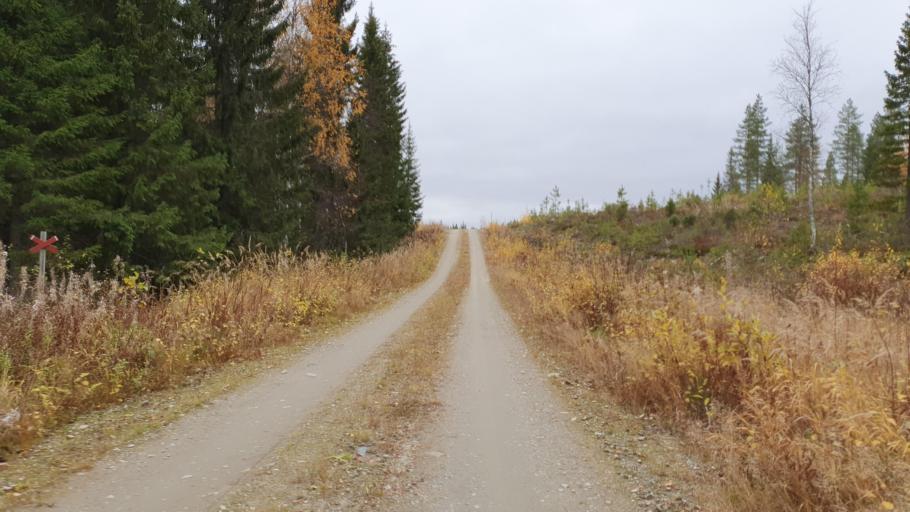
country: FI
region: Kainuu
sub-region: Kehys-Kainuu
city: Kuhmo
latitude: 64.4462
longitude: 29.6227
